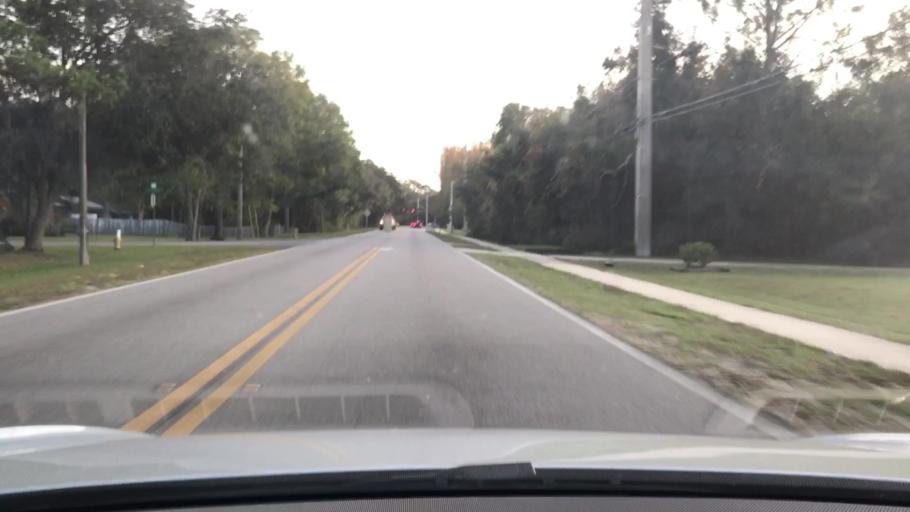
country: US
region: Florida
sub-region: Saint Johns County
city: Villano Beach
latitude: 29.9343
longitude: -81.3446
